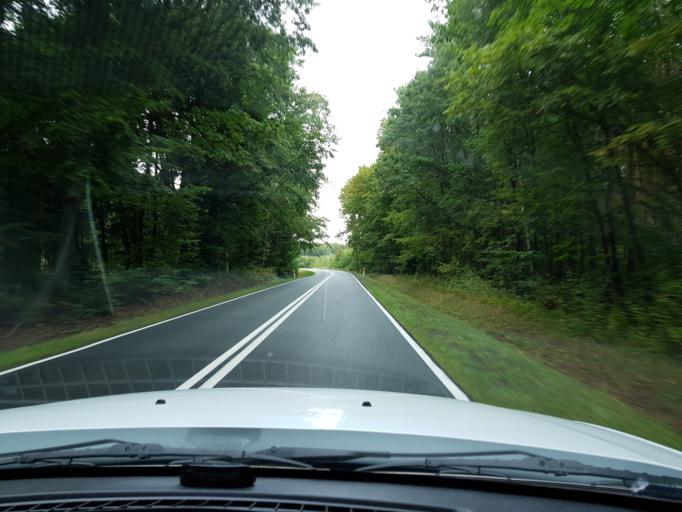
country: PL
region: West Pomeranian Voivodeship
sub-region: Powiat gryfinski
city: Widuchowa
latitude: 53.0807
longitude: 14.4286
